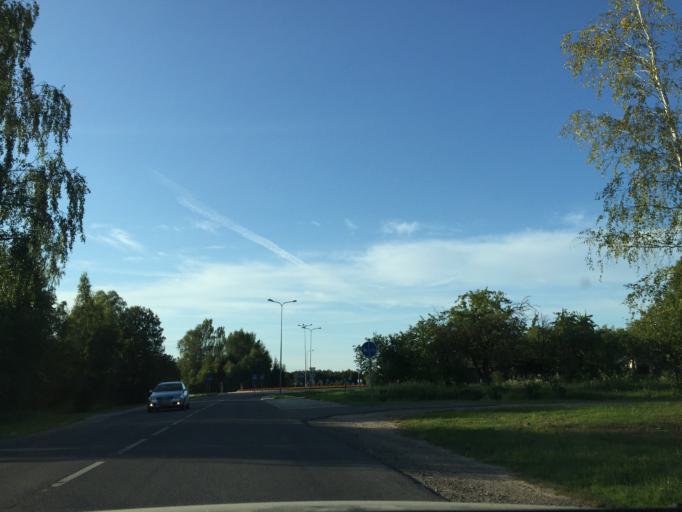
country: LT
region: Panevezys
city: Rokiskis
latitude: 55.9510
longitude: 25.5751
